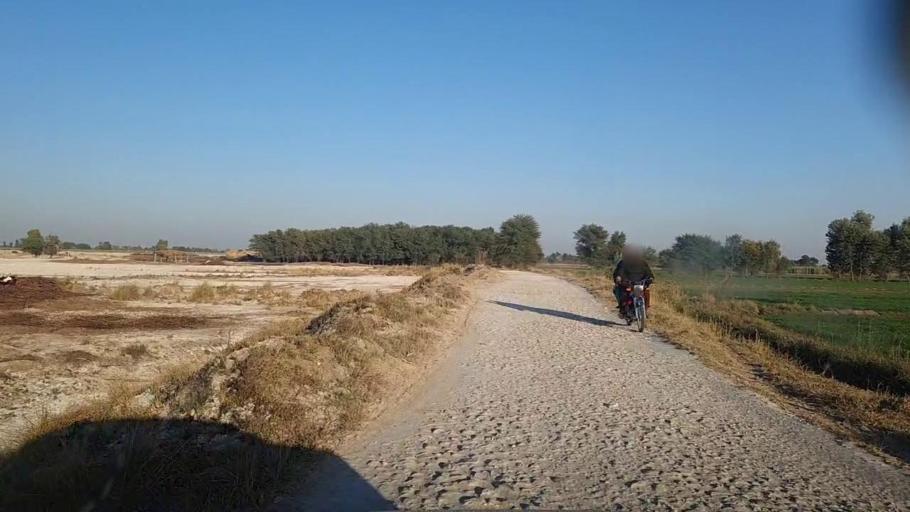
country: PK
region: Sindh
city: Khairpur
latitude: 28.0424
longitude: 69.7334
